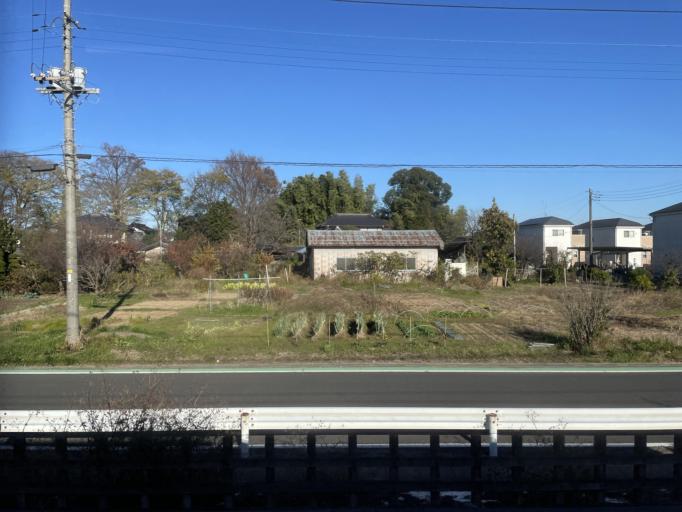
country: JP
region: Saitama
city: Kurihashi
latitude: 36.1083
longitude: 139.7183
